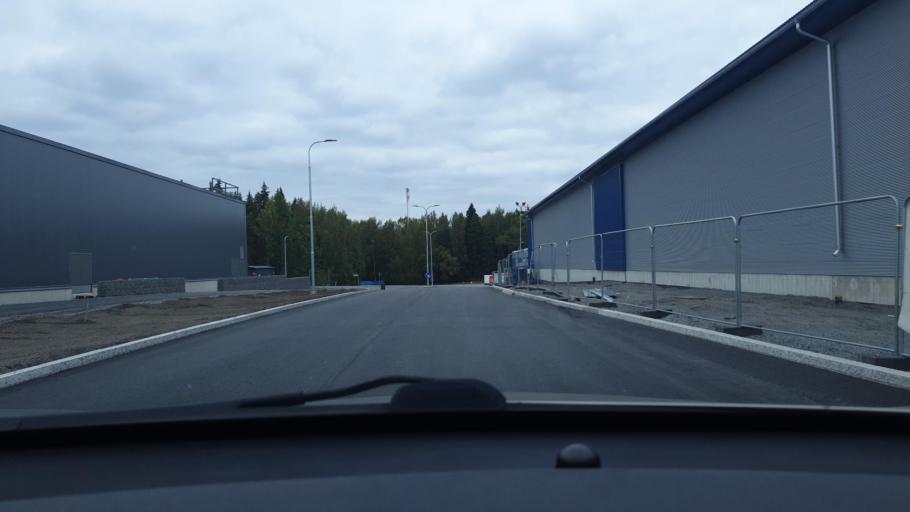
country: FI
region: Ostrobothnia
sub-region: Vaasa
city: Teeriniemi
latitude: 63.0730
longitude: 21.7003
